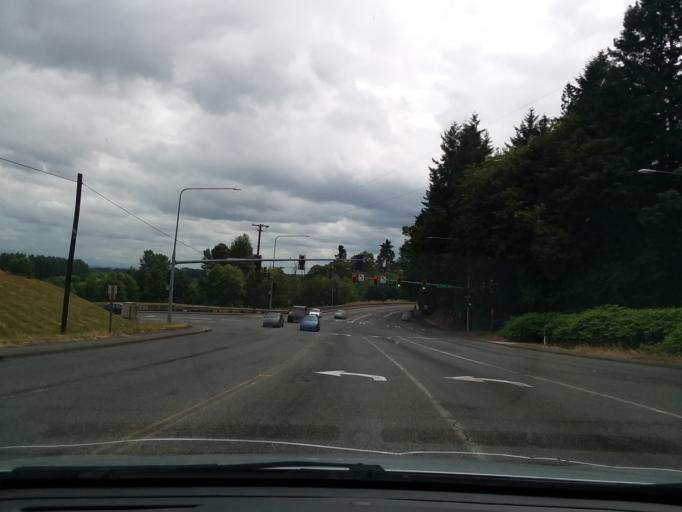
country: US
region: Washington
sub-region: King County
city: SeaTac
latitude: 47.4236
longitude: -122.2773
